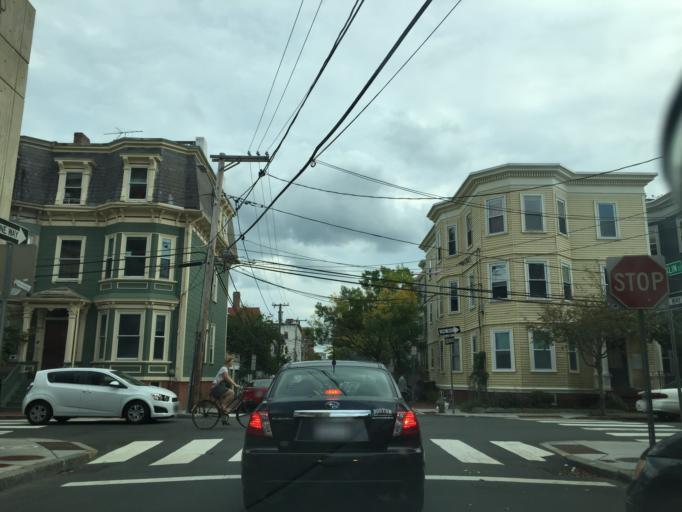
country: US
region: Massachusetts
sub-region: Middlesex County
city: Cambridge
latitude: 42.3638
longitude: -71.1039
